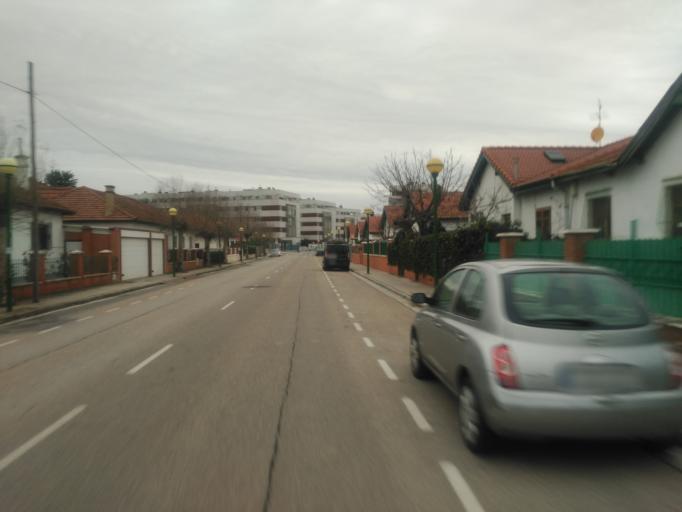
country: ES
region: Castille and Leon
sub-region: Provincia de Burgos
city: Villagonzalo-Pedernales
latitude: 42.3425
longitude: -3.7393
